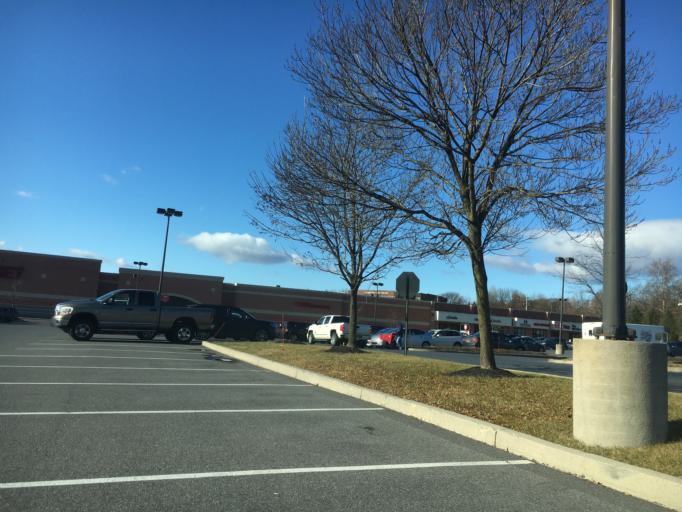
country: US
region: Pennsylvania
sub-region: Lehigh County
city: Dorneyville
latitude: 40.6133
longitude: -75.5341
